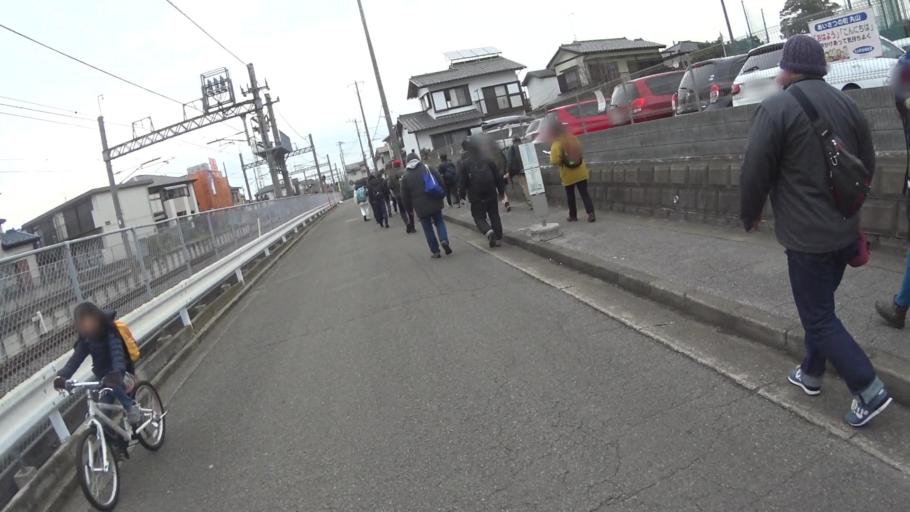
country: JP
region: Chiba
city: Funabashi
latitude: 35.7484
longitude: 139.9937
